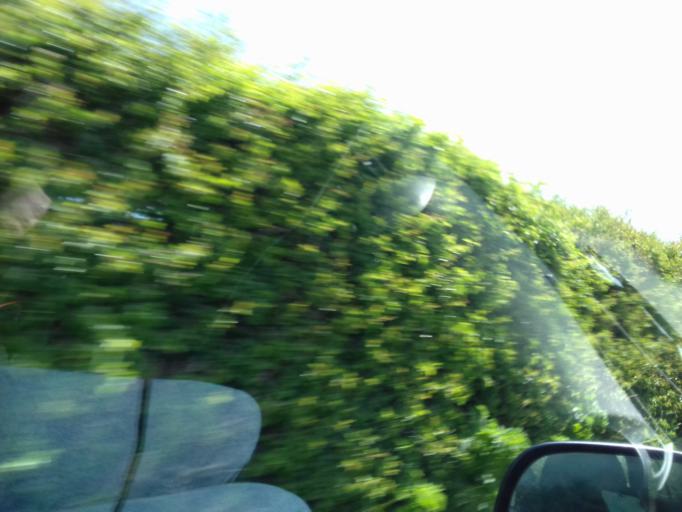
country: IE
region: Munster
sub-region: Waterford
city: Dunmore East
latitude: 52.2433
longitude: -6.8595
